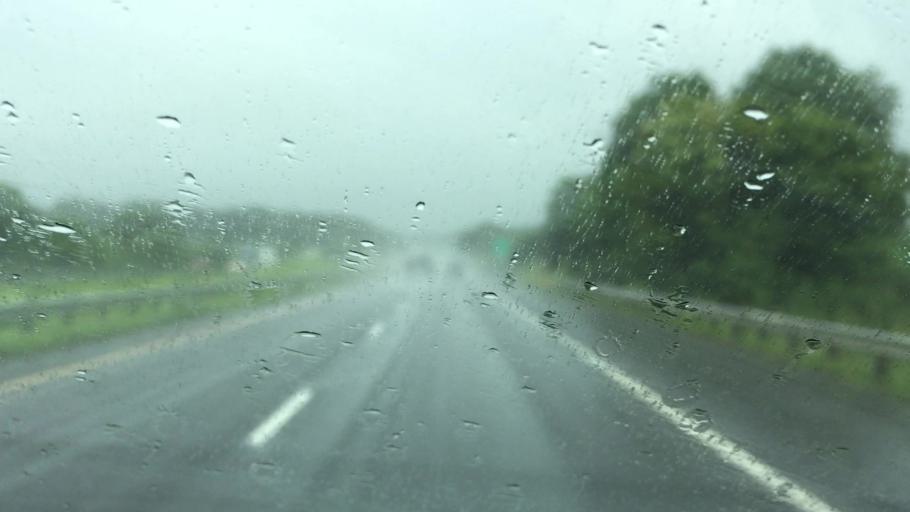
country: US
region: Maryland
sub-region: Washington County
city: Robinwood
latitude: 39.5946
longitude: -77.6552
